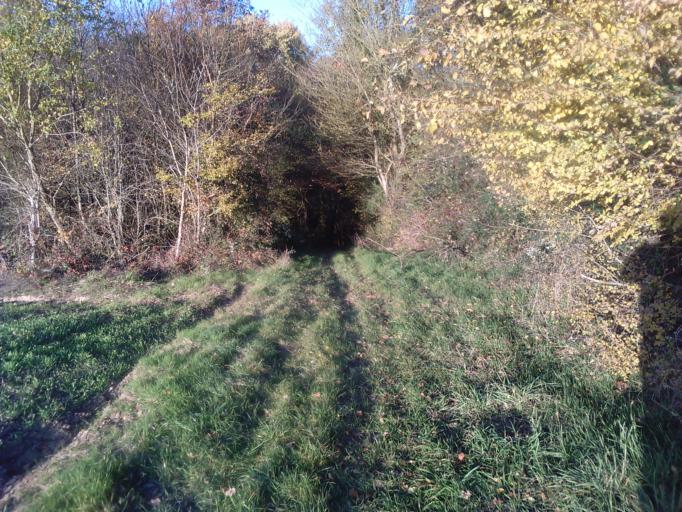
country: FR
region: Centre
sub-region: Departement du Loir-et-Cher
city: Villiers-sur-Loir
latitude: 47.8179
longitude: 0.9738
